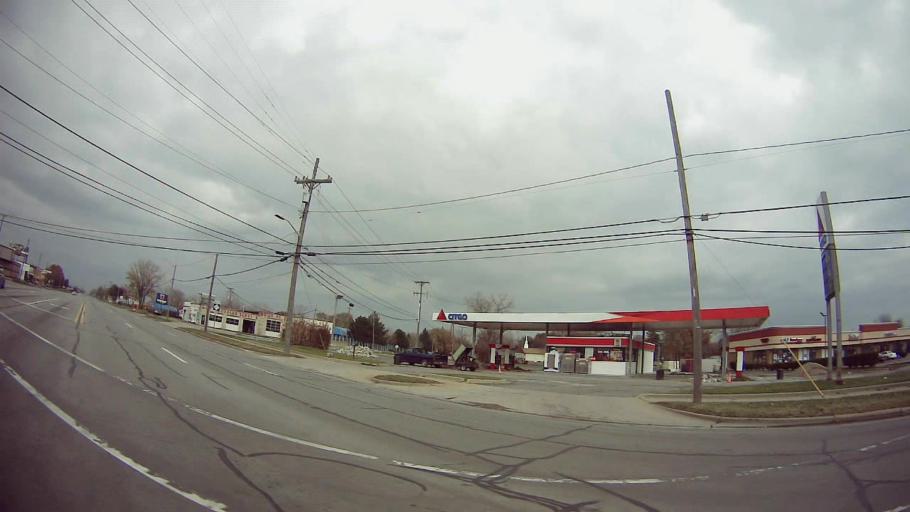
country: US
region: Michigan
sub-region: Macomb County
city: Eastpointe
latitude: 42.4692
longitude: -82.9863
